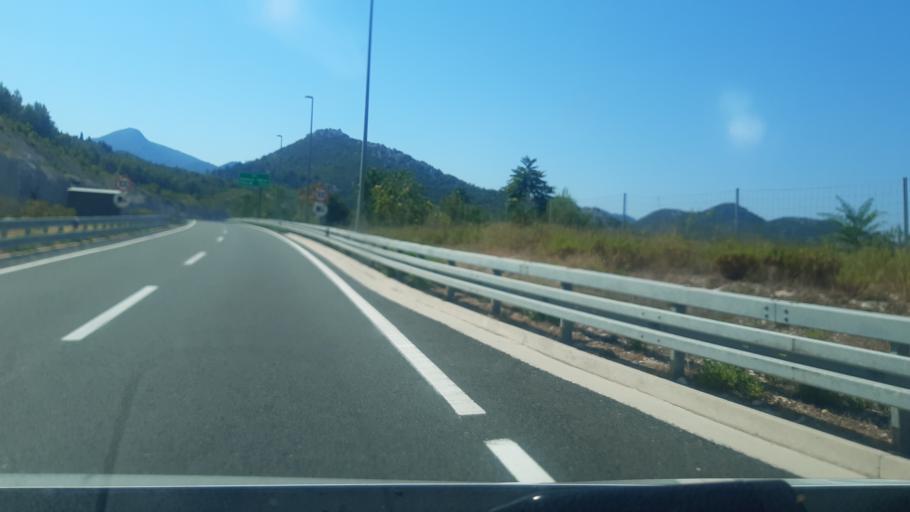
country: BA
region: Federation of Bosnia and Herzegovina
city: Ljubuski
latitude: 43.1353
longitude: 17.4830
